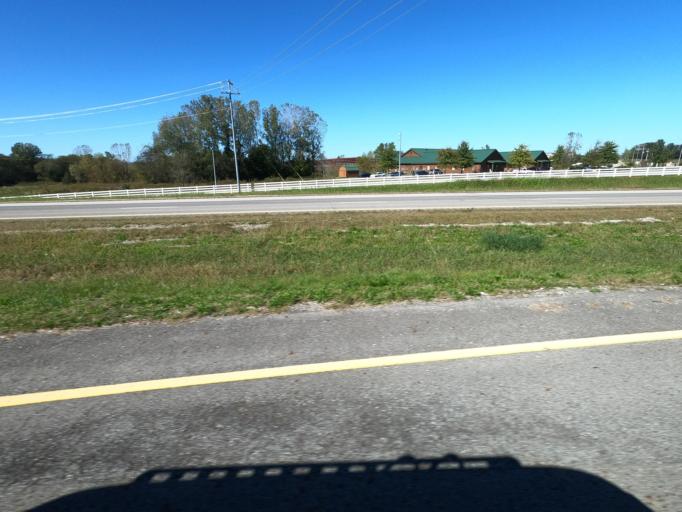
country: US
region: Tennessee
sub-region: Maury County
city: Mount Pleasant
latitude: 35.5650
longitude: -87.1726
